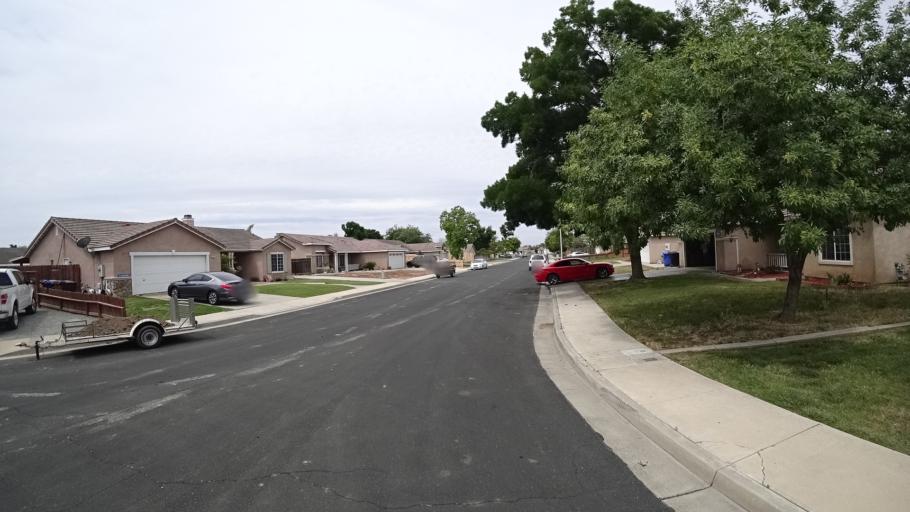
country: US
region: California
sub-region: Kings County
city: Lucerne
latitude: 36.3669
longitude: -119.6374
